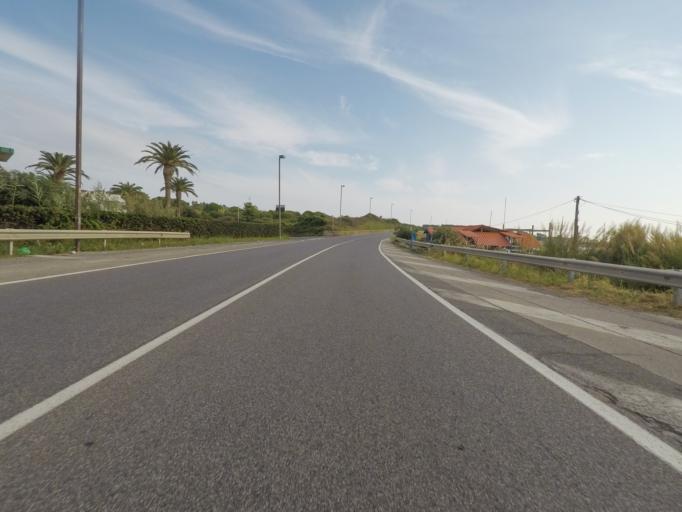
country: IT
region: Latium
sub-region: Citta metropolitana di Roma Capitale
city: Santa Marinella
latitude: 42.0383
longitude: 11.8320
